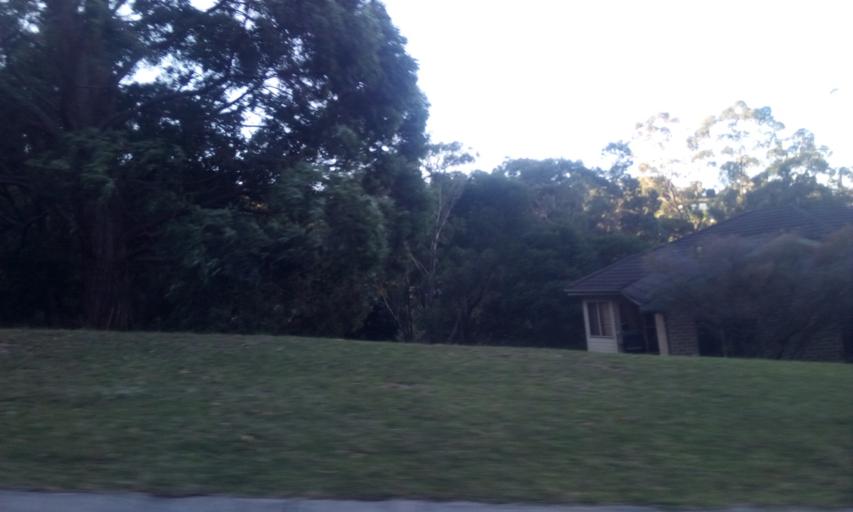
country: AU
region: New South Wales
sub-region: Wollongong
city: Mount Keira
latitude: -34.4232
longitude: 150.8447
